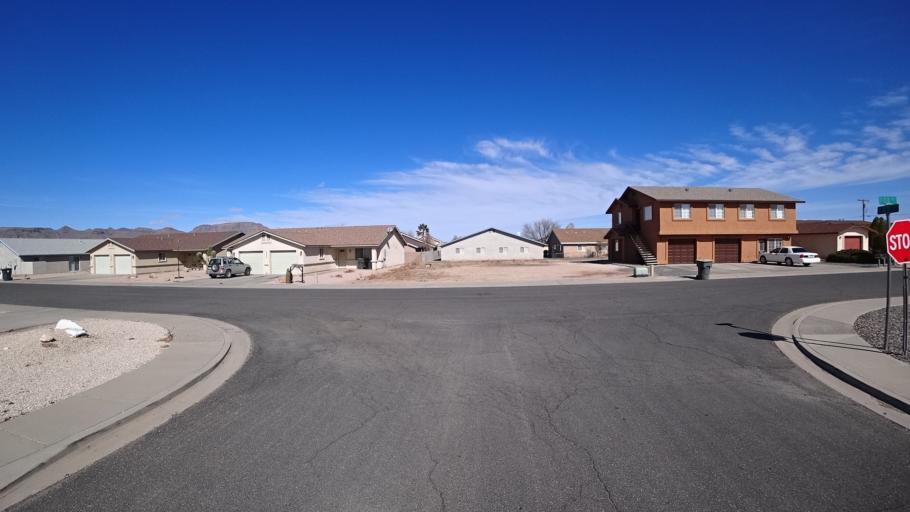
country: US
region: Arizona
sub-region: Mohave County
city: Kingman
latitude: 35.2201
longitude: -114.0213
